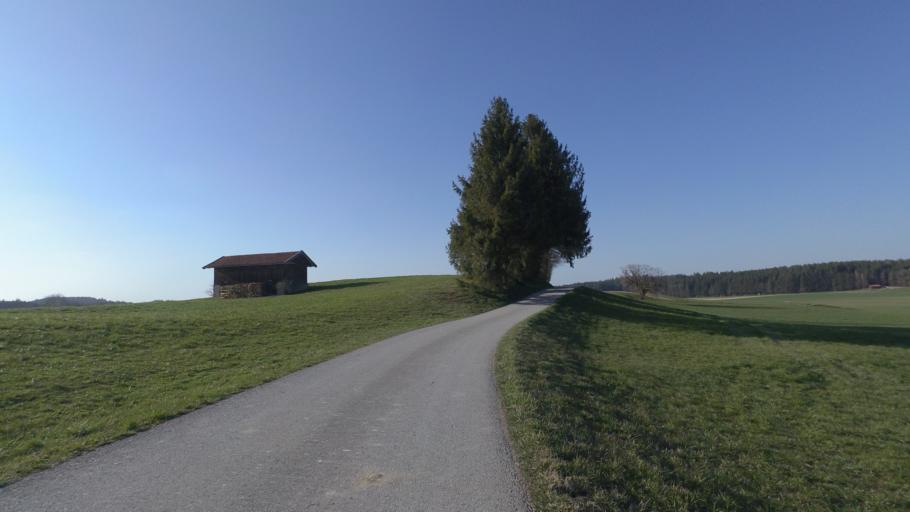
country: DE
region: Bavaria
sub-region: Upper Bavaria
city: Traunreut
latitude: 47.9355
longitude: 12.5598
